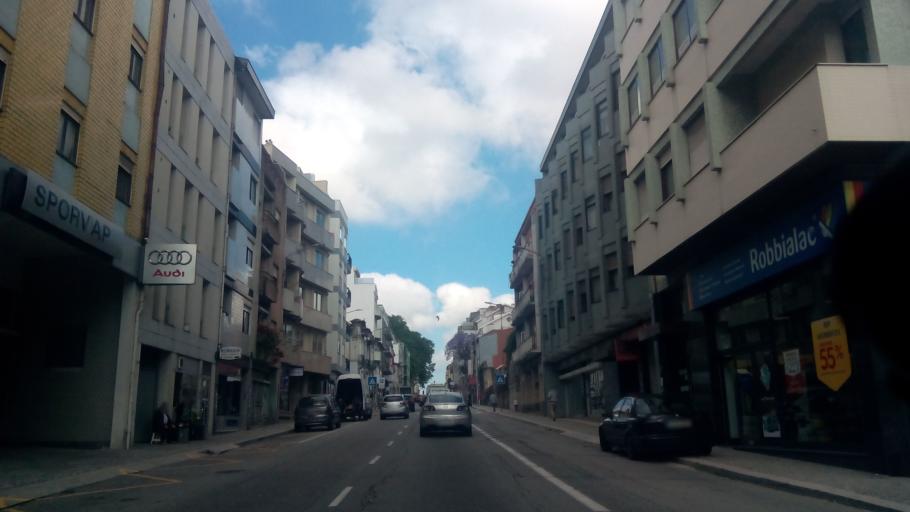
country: PT
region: Porto
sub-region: Porto
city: Porto
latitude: 41.1614
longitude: -8.6008
